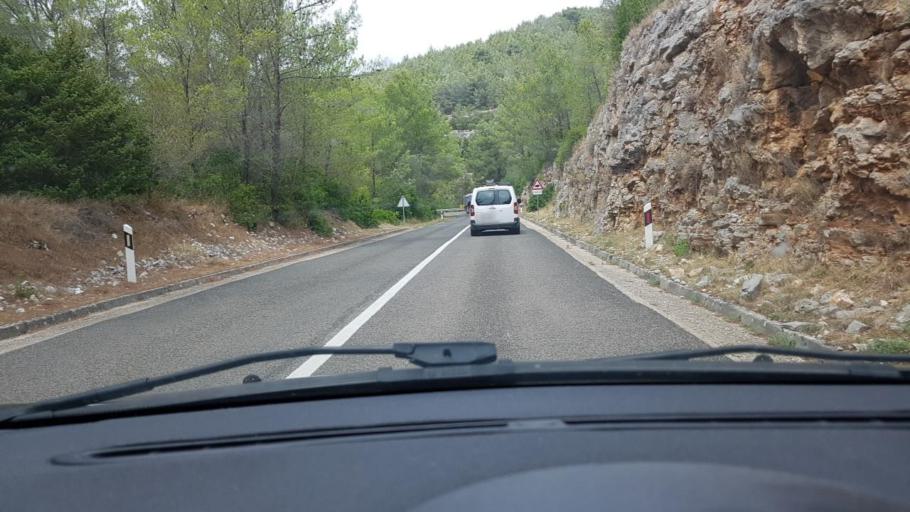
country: HR
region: Dubrovacko-Neretvanska
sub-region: Grad Dubrovnik
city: Vela Luka
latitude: 42.9492
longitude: 16.7916
